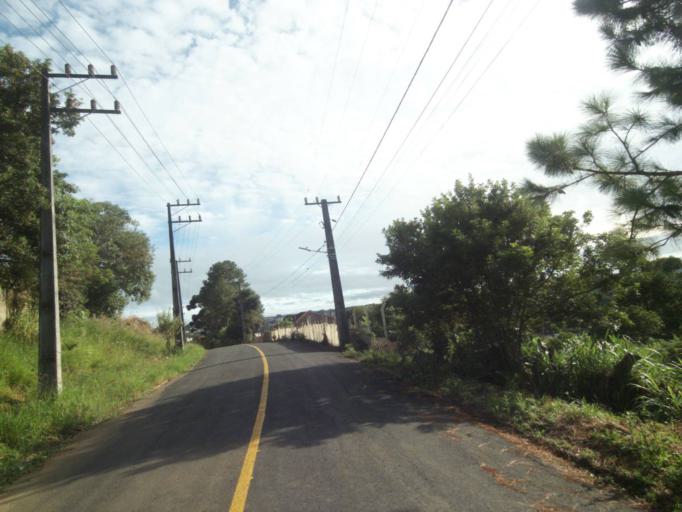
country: BR
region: Parana
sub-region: Telemaco Borba
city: Telemaco Borba
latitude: -24.3434
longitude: -50.6178
